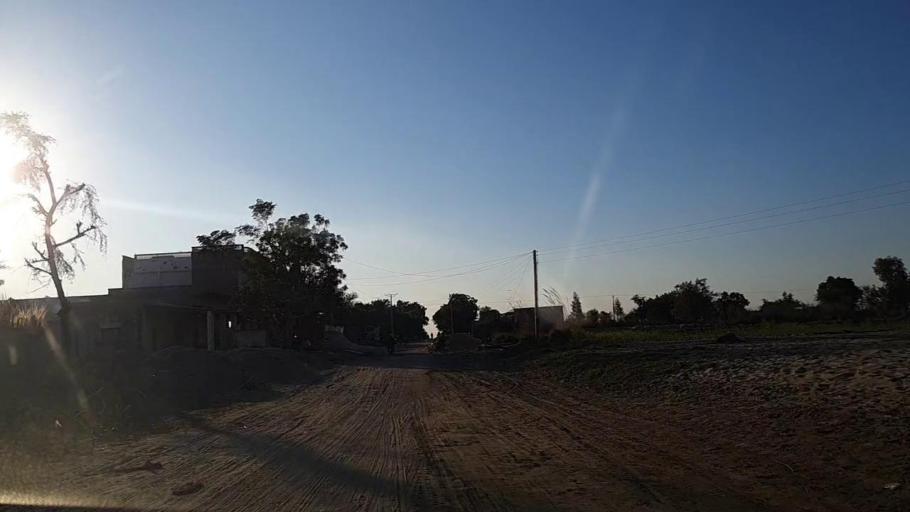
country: PK
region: Sindh
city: Khadro
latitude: 26.2791
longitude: 68.8312
